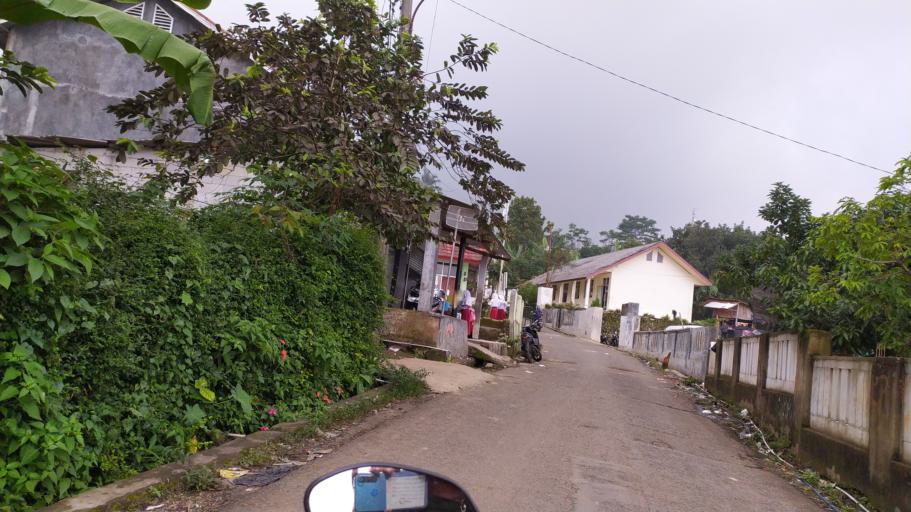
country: ID
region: West Java
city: Ciampea
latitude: -6.6478
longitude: 106.7046
